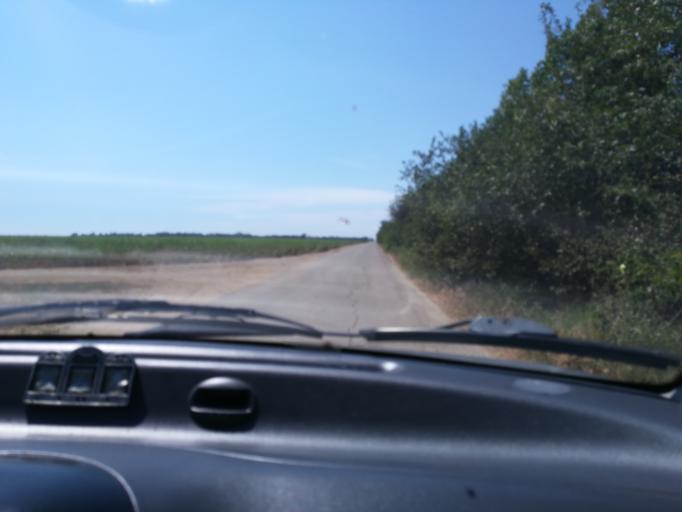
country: RU
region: Krasnodarskiy
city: Blagovetschenskaya
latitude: 45.0587
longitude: 37.1000
